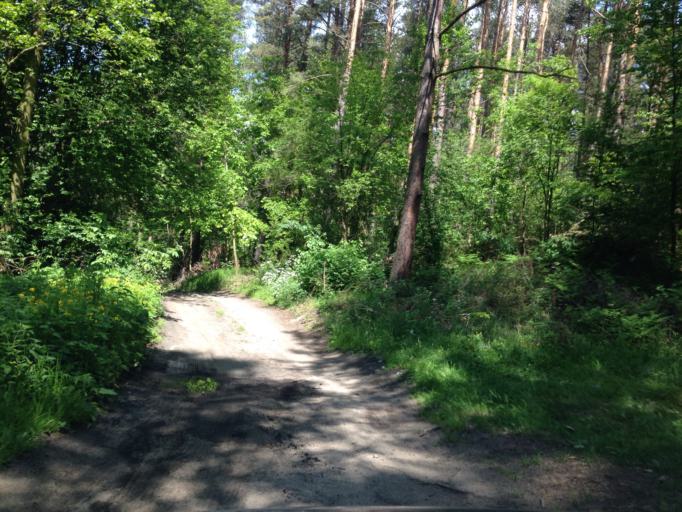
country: PL
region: Kujawsko-Pomorskie
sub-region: Powiat brodnicki
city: Brodnica
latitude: 53.3280
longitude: 19.3591
